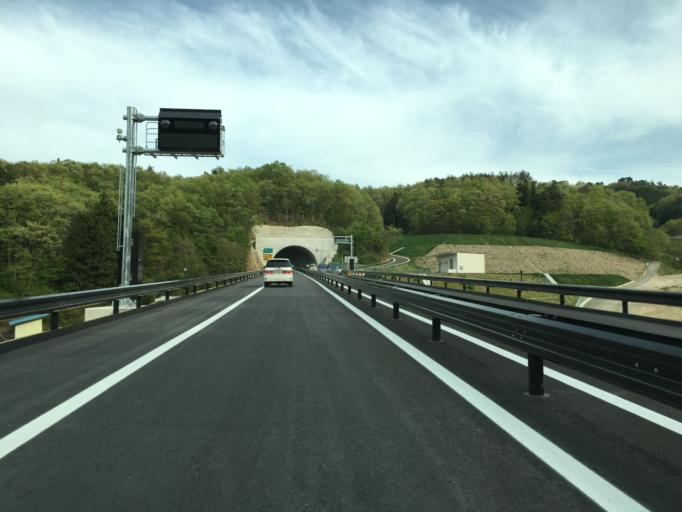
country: JP
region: Fukushima
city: Hobaramachi
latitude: 37.7838
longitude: 140.5685
